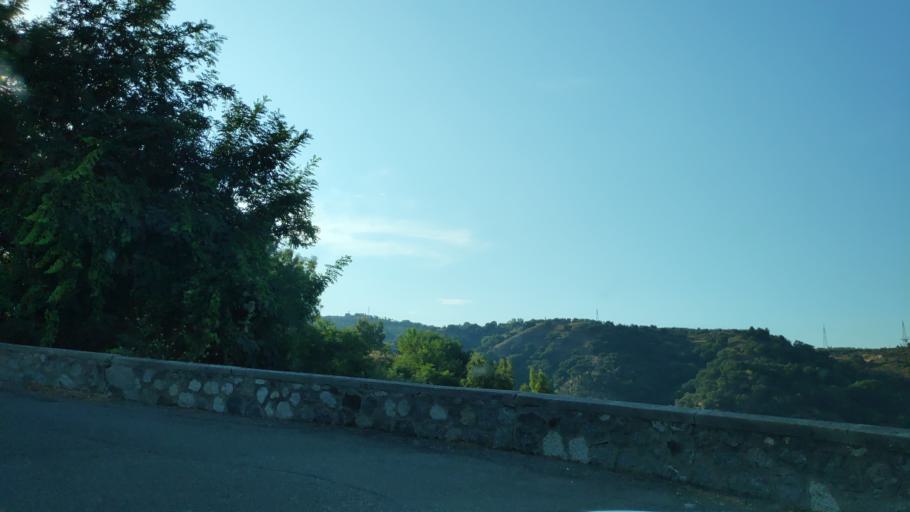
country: IT
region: Calabria
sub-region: Provincia di Catanzaro
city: Satriano
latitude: 38.6707
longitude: 16.4825
